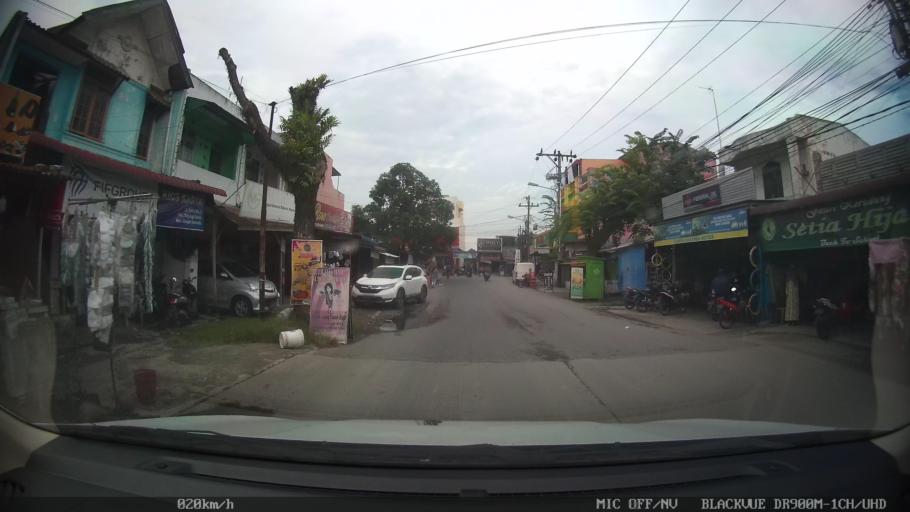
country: ID
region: North Sumatra
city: Sunggal
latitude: 3.6090
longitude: 98.6088
